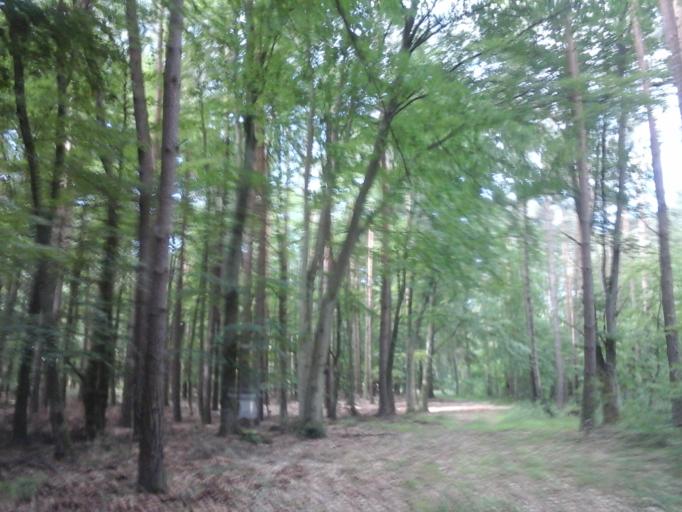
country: PL
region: West Pomeranian Voivodeship
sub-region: Powiat choszczenski
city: Choszczno
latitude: 53.2307
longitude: 15.4456
